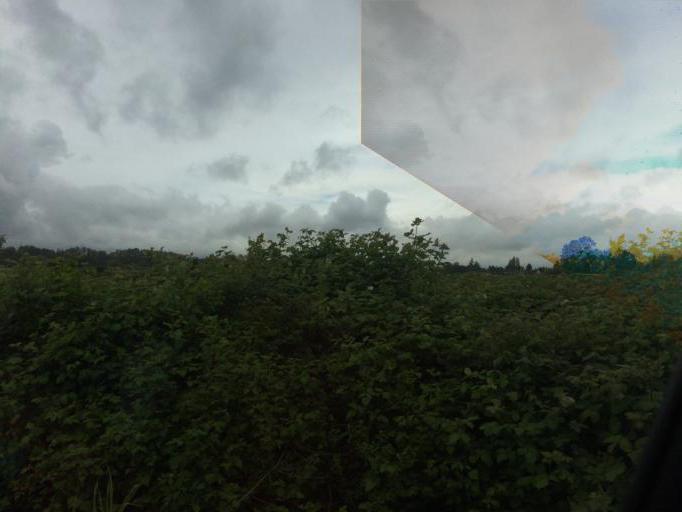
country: CA
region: British Columbia
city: Ladner
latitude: 49.1322
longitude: -123.1033
